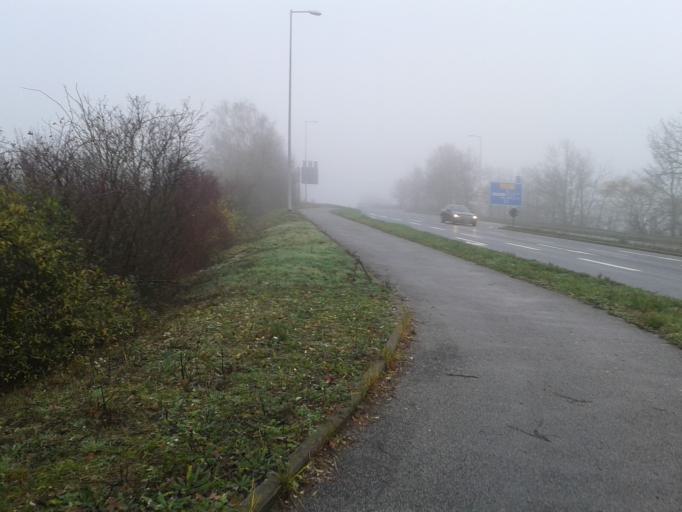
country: DE
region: Bavaria
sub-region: Upper Franconia
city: Bamberg
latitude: 49.9210
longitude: 10.8992
